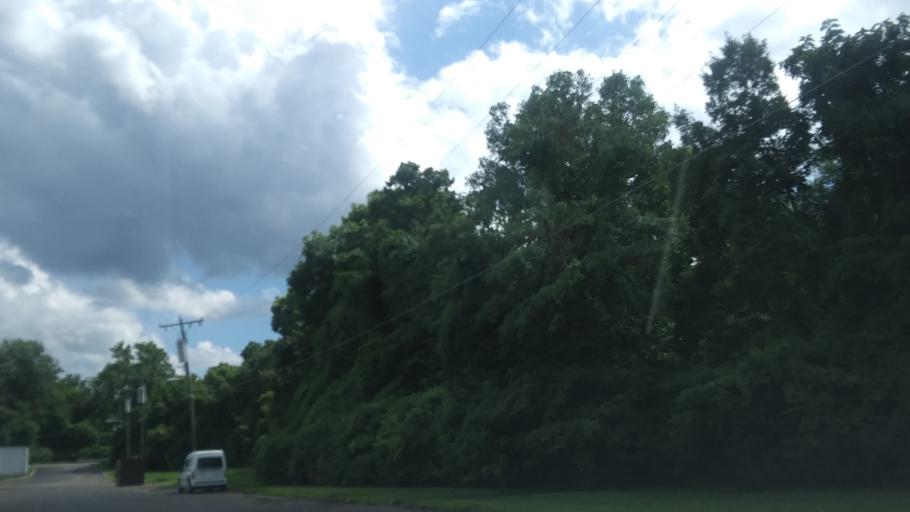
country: US
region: Tennessee
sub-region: Davidson County
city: Oak Hill
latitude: 36.0910
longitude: -86.6993
